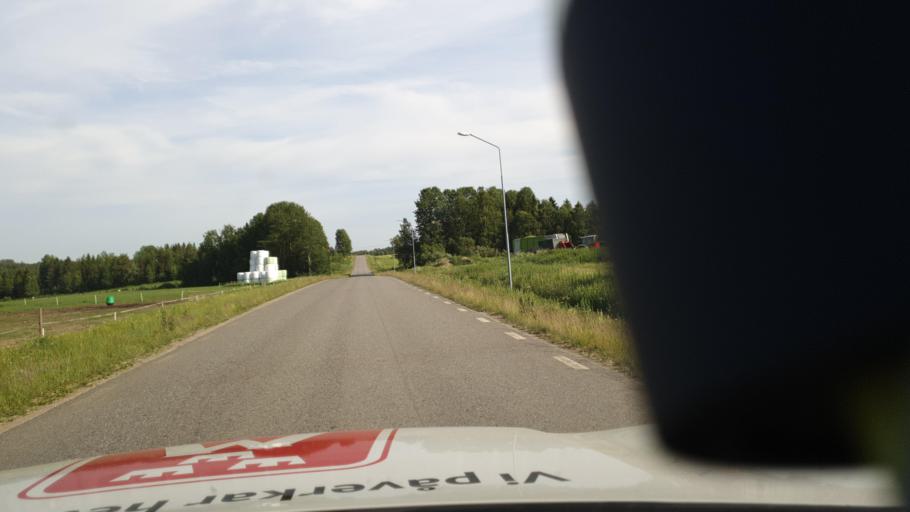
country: SE
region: Vaesterbotten
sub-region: Robertsfors Kommun
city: Robertsfors
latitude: 64.3694
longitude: 20.9133
